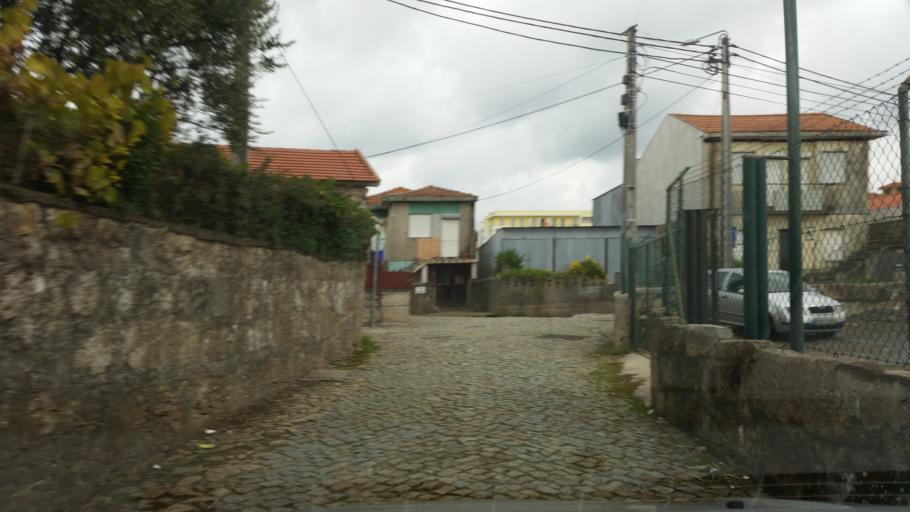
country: PT
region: Porto
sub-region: Valongo
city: Alfena
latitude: 41.2381
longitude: -8.5334
